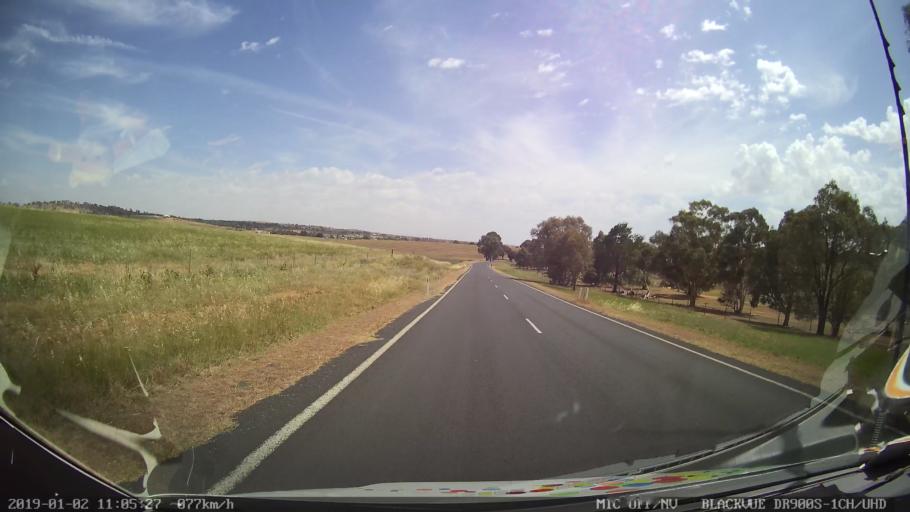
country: AU
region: New South Wales
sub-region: Young
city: Young
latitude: -34.5646
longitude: 148.3539
